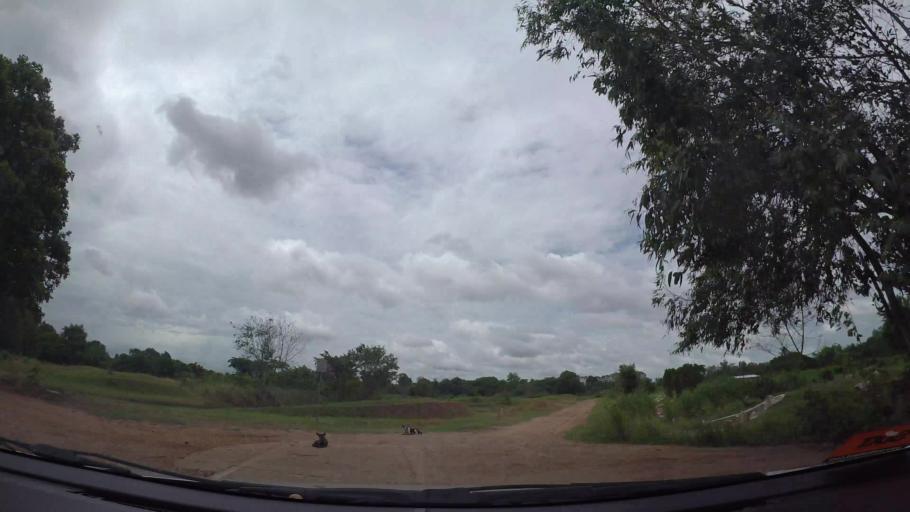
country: TH
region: Chon Buri
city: Si Racha
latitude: 13.1862
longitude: 100.9623
